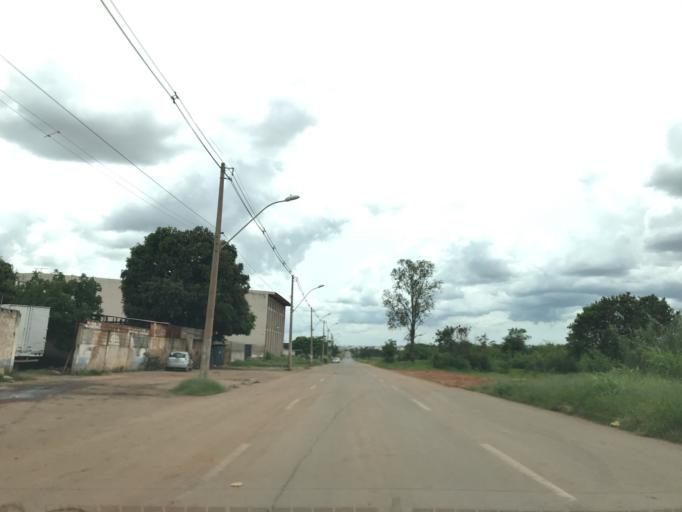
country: BR
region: Federal District
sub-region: Brasilia
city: Brasilia
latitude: -15.7930
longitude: -47.9905
